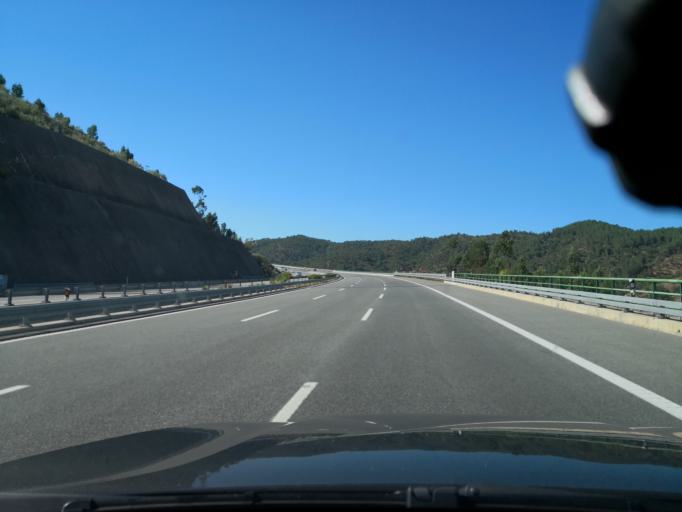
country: PT
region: Faro
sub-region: Silves
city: Sao Bartolomeu de Messines
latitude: 37.3841
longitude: -8.2625
